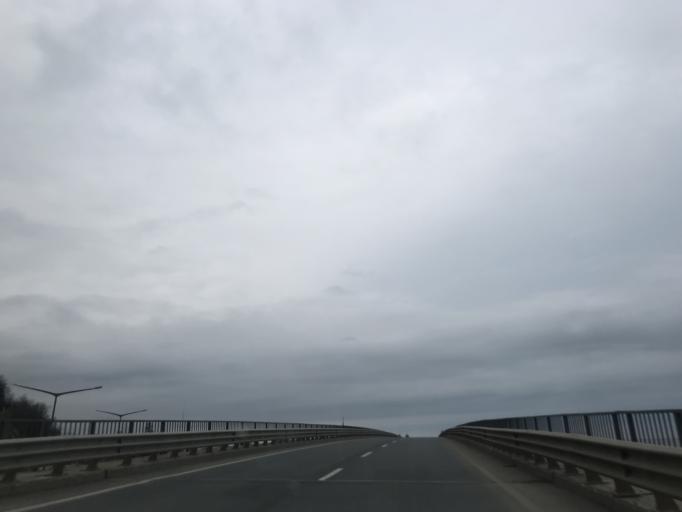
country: TR
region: Trabzon
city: Akcaabat
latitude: 41.0016
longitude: 39.6365
